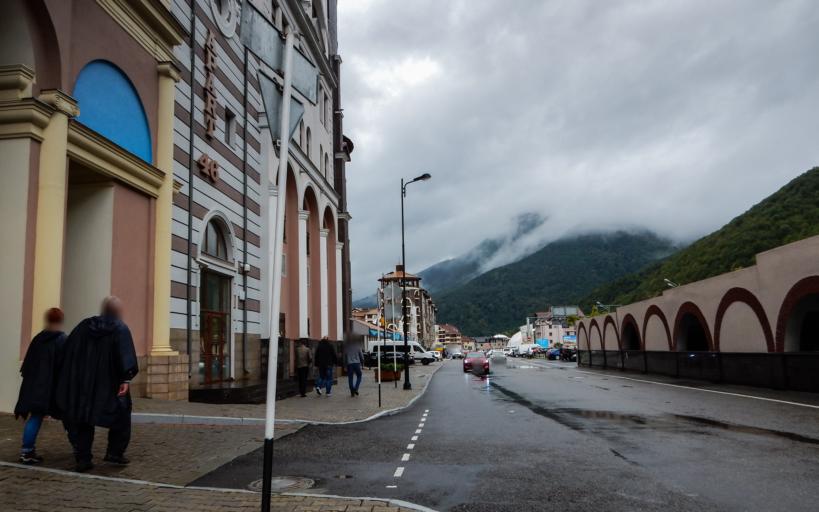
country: RU
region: Krasnodarskiy
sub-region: Sochi City
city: Krasnaya Polyana
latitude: 43.6829
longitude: 40.2692
